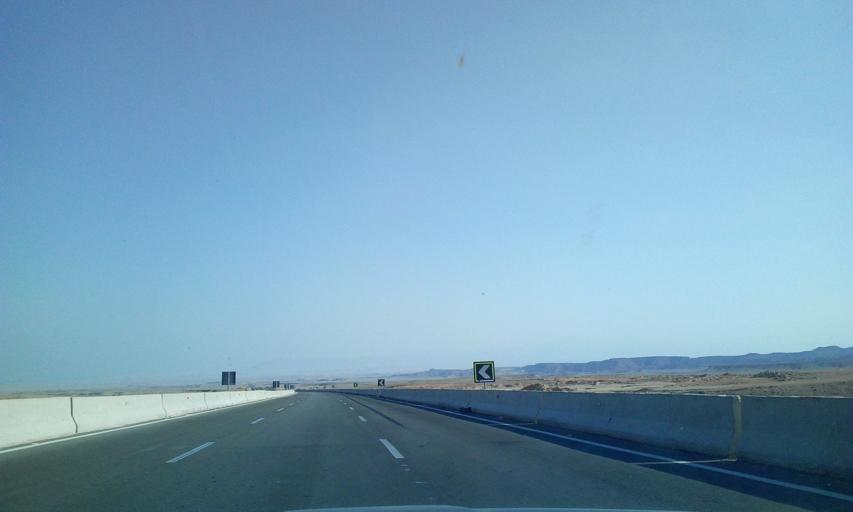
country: EG
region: As Suways
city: Ain Sukhna
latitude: 29.2719
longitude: 32.4700
